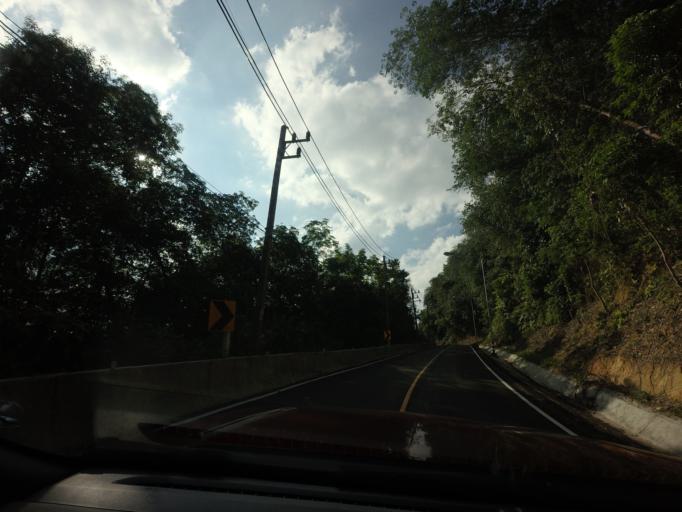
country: TH
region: Yala
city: Than To
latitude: 6.1344
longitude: 101.2966
